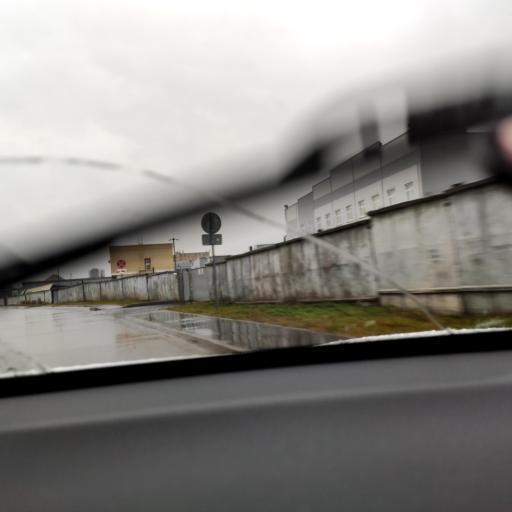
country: RU
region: Tatarstan
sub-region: Gorod Kazan'
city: Kazan
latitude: 55.8668
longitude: 49.1094
